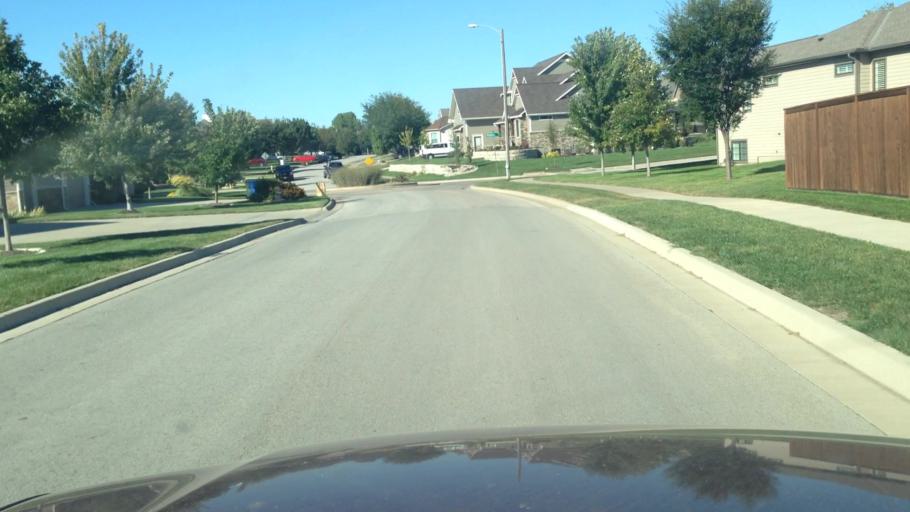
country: US
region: Kansas
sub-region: Douglas County
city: Lawrence
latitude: 38.9618
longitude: -95.3216
